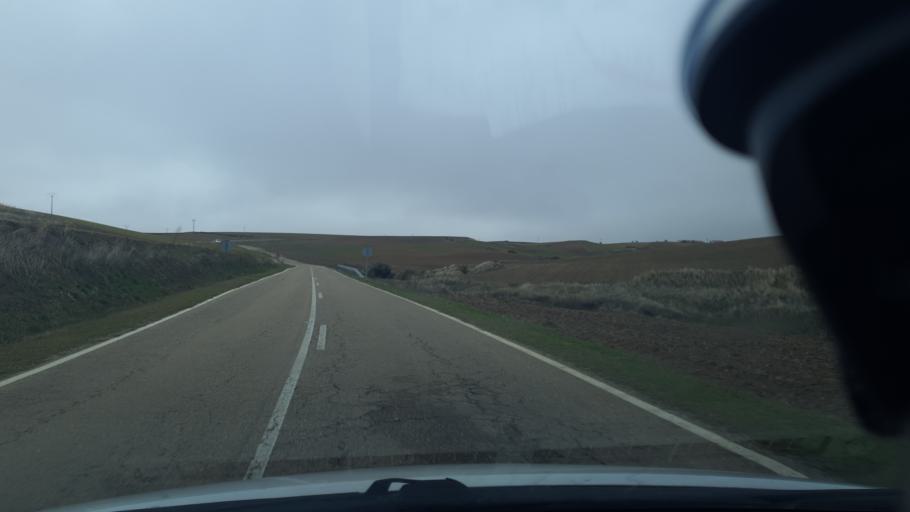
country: ES
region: Castille and Leon
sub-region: Provincia de Segovia
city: Hontanares de Eresma
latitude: 40.9877
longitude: -4.2010
